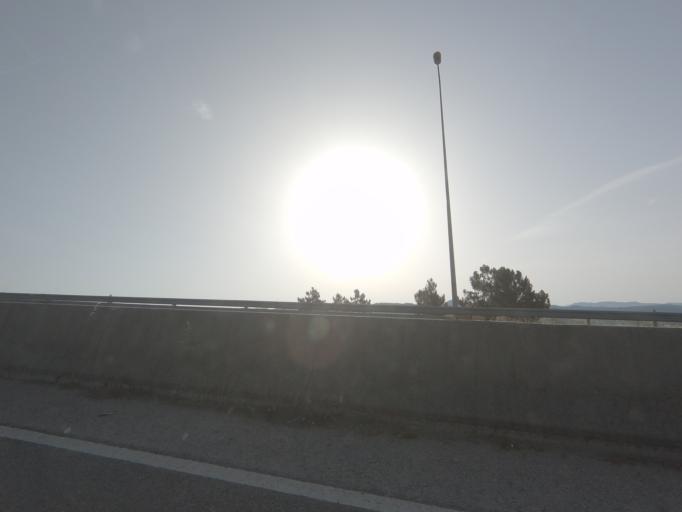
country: PT
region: Vila Real
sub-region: Sabrosa
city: Sabrosa
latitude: 41.2841
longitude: -7.4736
